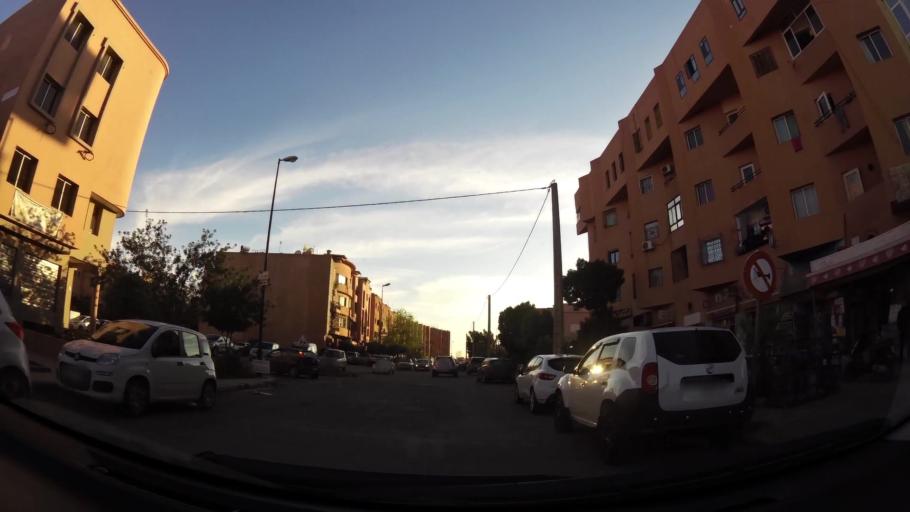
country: MA
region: Marrakech-Tensift-Al Haouz
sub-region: Marrakech
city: Marrakesh
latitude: 31.6233
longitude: -8.0303
